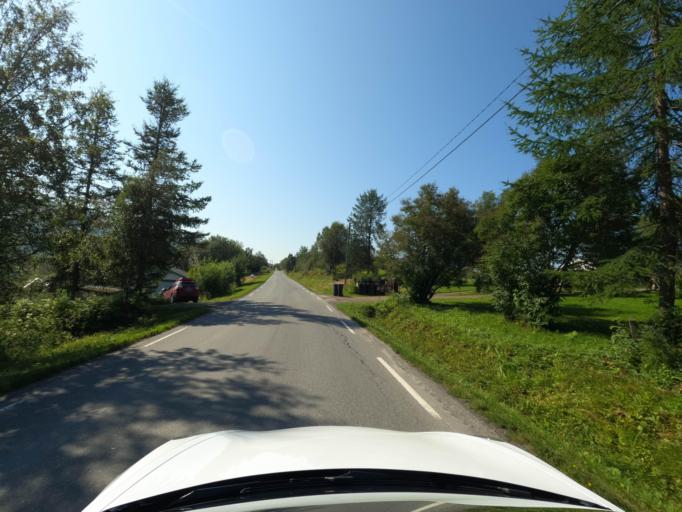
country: NO
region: Nordland
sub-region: Ballangen
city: Ballangen
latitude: 68.3549
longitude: 16.8660
